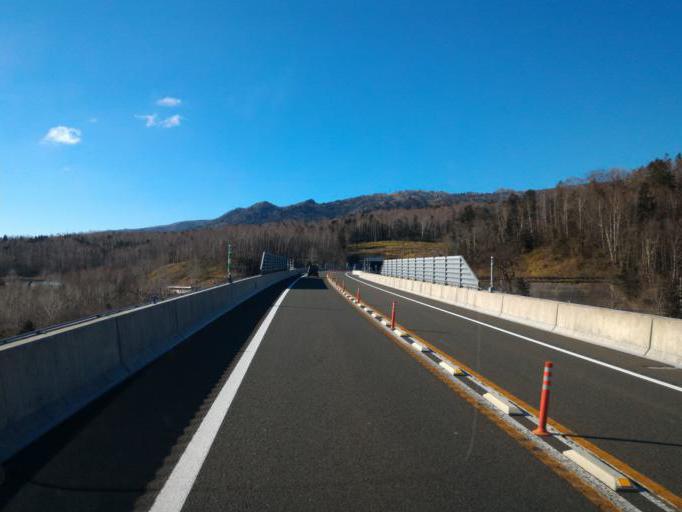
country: JP
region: Hokkaido
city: Shimo-furano
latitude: 42.9517
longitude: 142.3118
